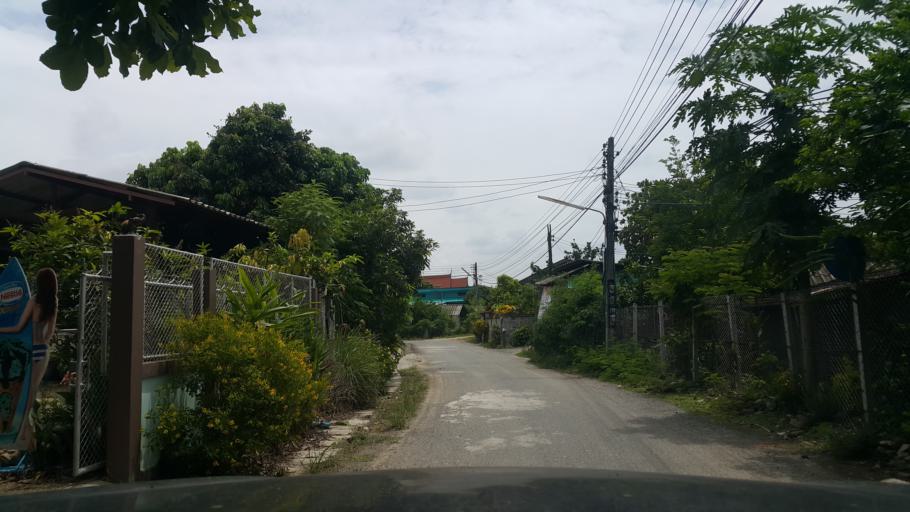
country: TH
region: Chiang Mai
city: San Kamphaeng
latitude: 18.6944
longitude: 99.1621
